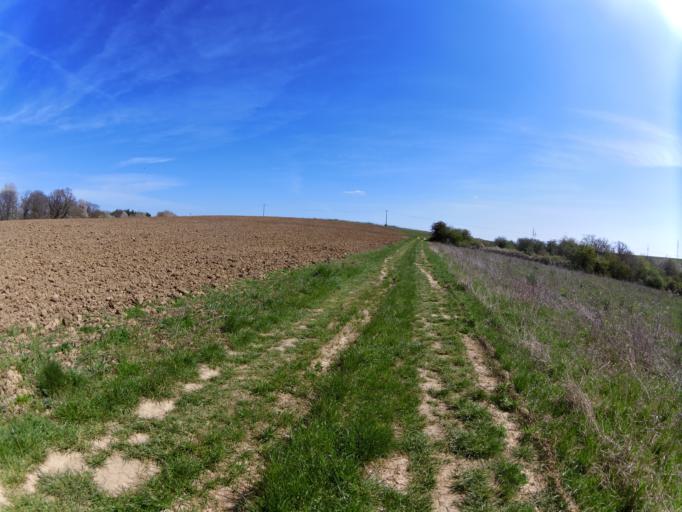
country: DE
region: Bavaria
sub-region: Regierungsbezirk Unterfranken
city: Greussenheim
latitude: 49.8141
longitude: 9.7779
